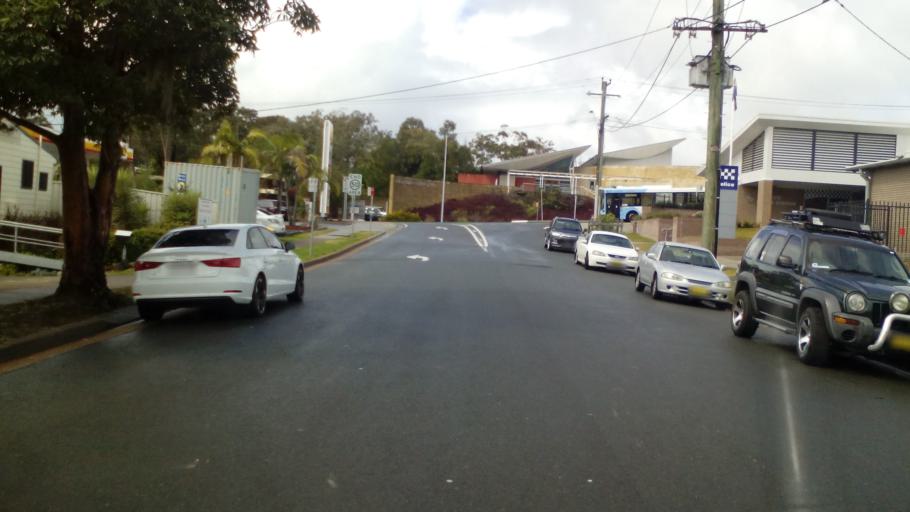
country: AU
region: New South Wales
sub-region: Lake Macquarie Shire
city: Toronto
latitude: -33.0120
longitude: 151.5925
